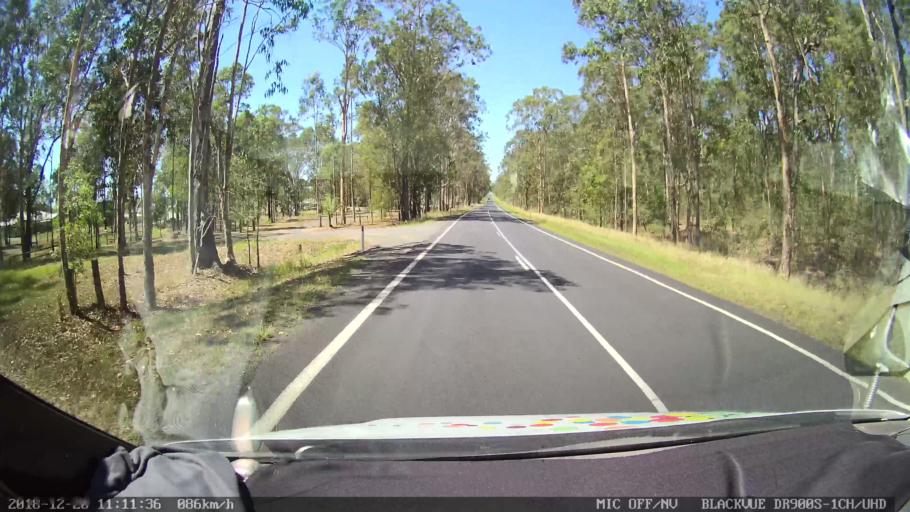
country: AU
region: New South Wales
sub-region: Richmond Valley
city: Casino
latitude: -28.9630
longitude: 153.0133
